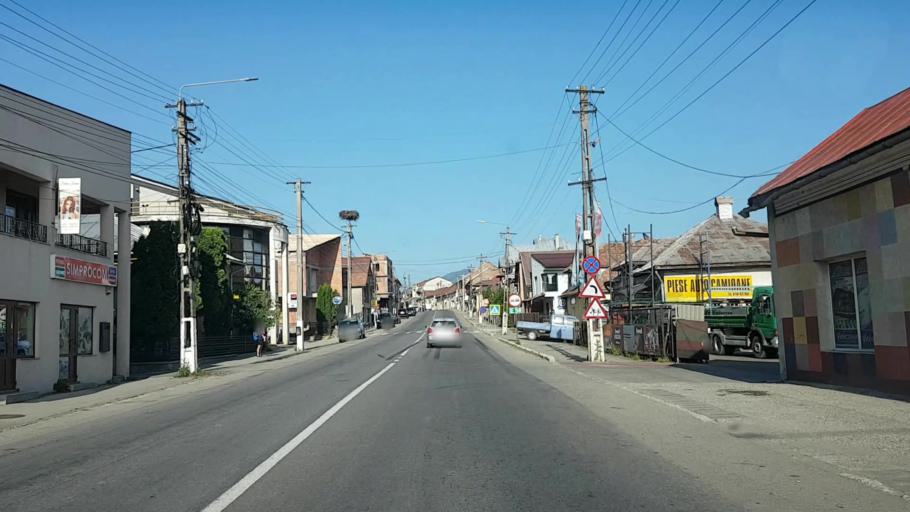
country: RO
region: Bistrita-Nasaud
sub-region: Comuna Prundu Bargaului
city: Susenii Bargaului
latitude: 47.2197
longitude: 24.7356
